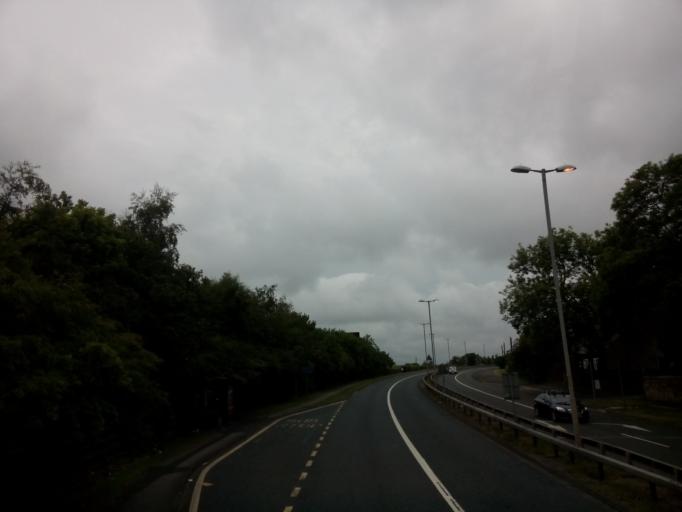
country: GB
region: England
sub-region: Gateshead
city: Lamesley
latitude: 54.9124
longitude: -1.5855
